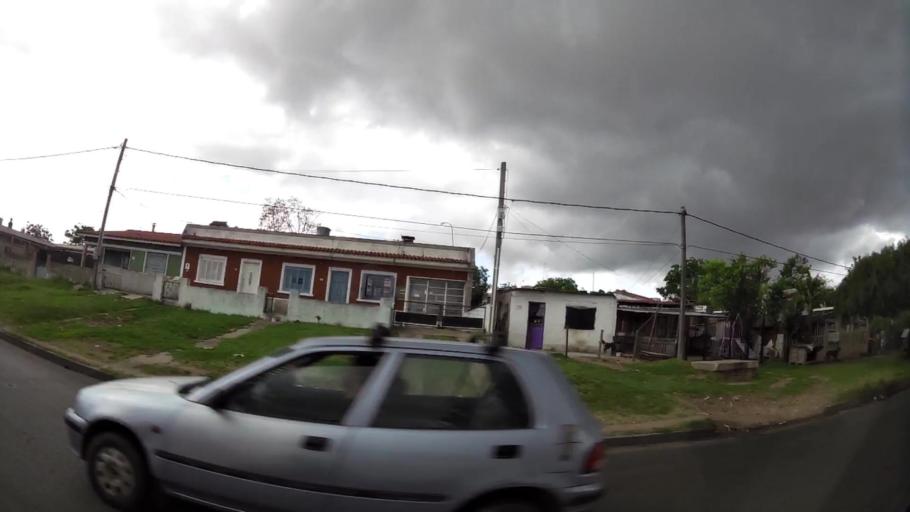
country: UY
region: Montevideo
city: Montevideo
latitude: -34.8417
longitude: -56.1692
